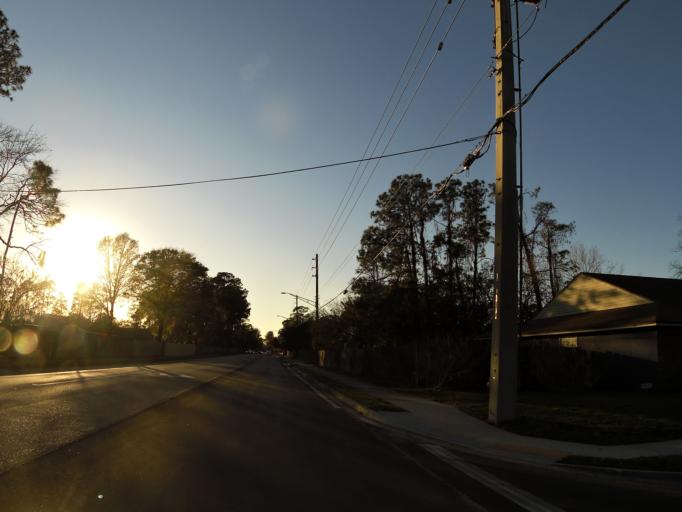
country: US
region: Florida
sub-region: Saint Johns County
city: Fruit Cove
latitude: 30.1723
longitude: -81.5923
